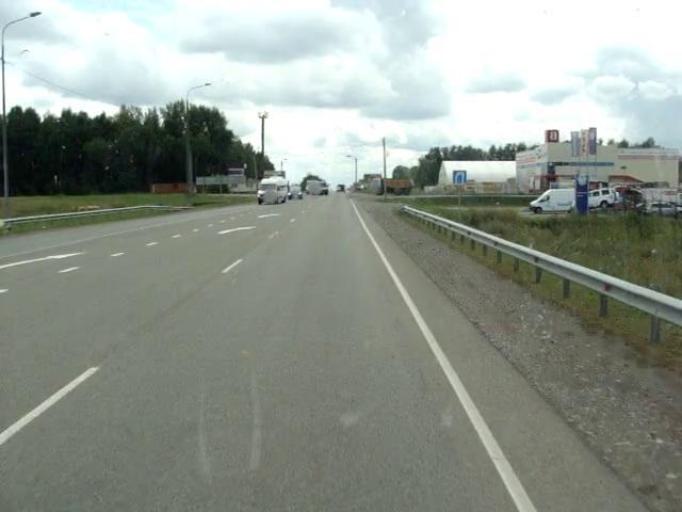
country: RU
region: Altai Krai
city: Zarya
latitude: 52.5760
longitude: 85.1798
